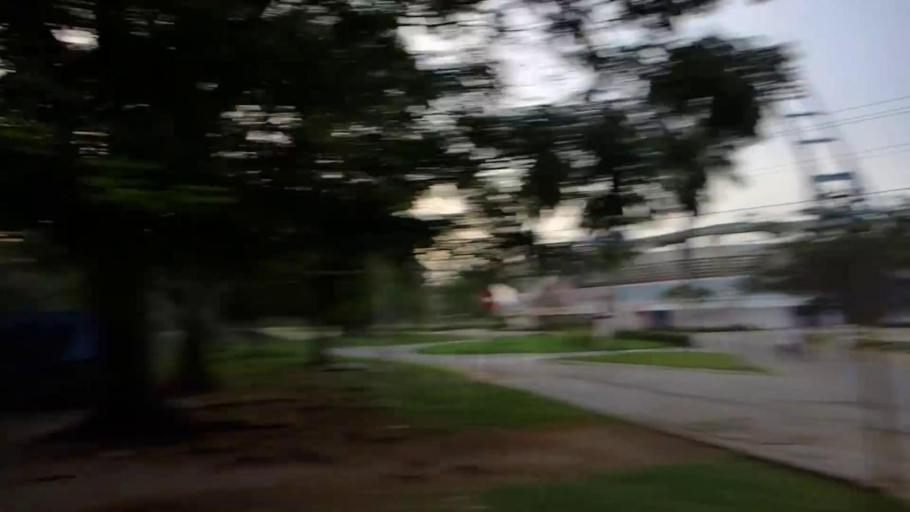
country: CU
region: Camaguey
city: Camaguey
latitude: 21.3775
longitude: -77.9107
